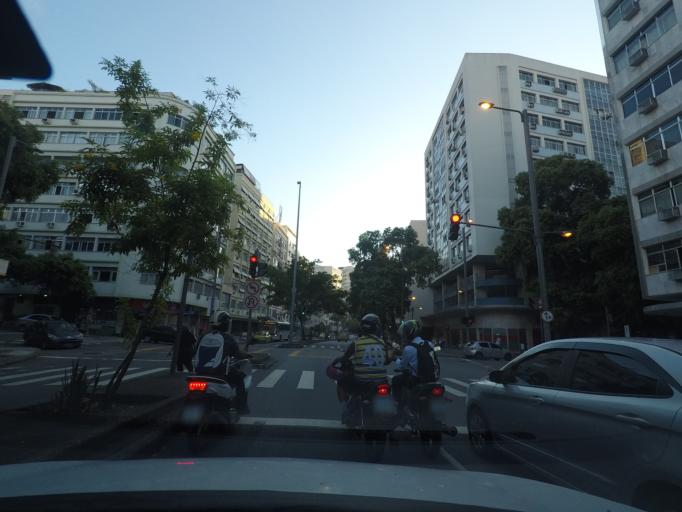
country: BR
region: Rio de Janeiro
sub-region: Rio De Janeiro
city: Rio de Janeiro
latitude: -22.9297
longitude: -43.2373
